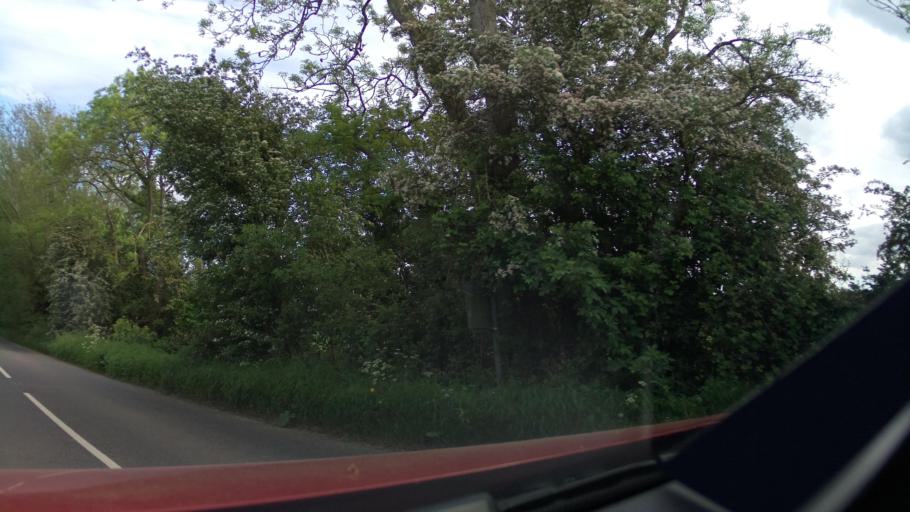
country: GB
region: England
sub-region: Gloucestershire
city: Chipping Campden
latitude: 52.0515
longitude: -1.7504
